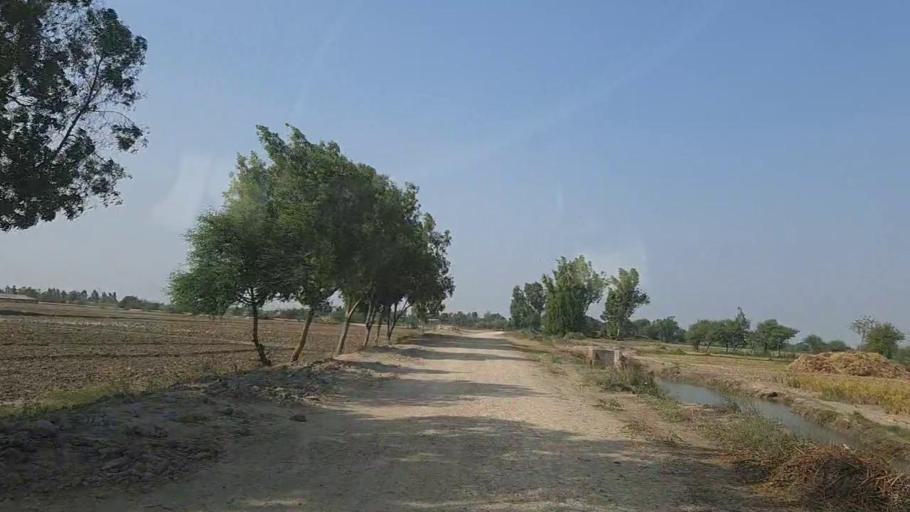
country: PK
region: Sindh
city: Mirpur Sakro
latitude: 24.5661
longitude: 67.8269
